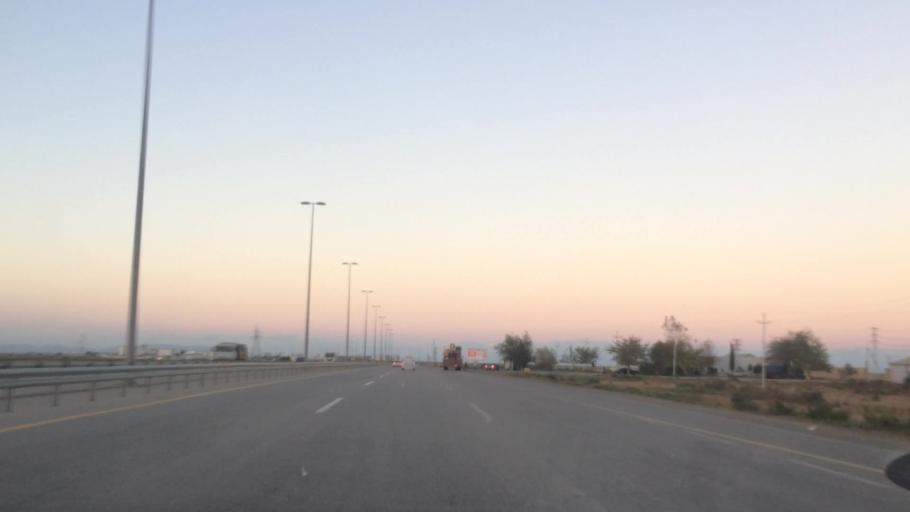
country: AZ
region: Baki
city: Qobustan
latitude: 39.9868
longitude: 49.4272
